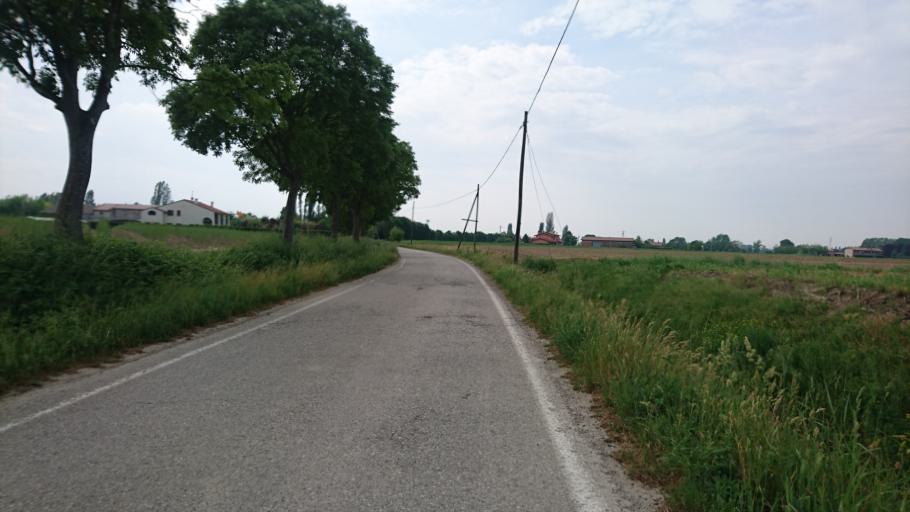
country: IT
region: Veneto
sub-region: Provincia di Padova
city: Pernumia
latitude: 45.2503
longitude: 11.7850
